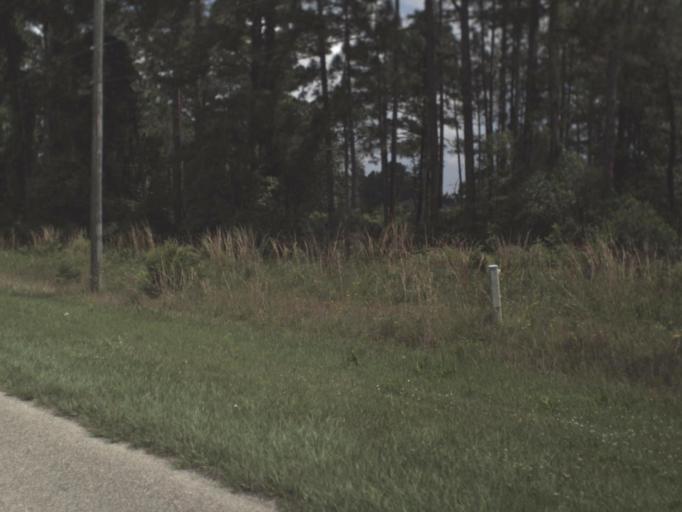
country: US
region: Florida
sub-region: Saint Johns County
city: Villano Beach
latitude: 30.0311
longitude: -81.4087
